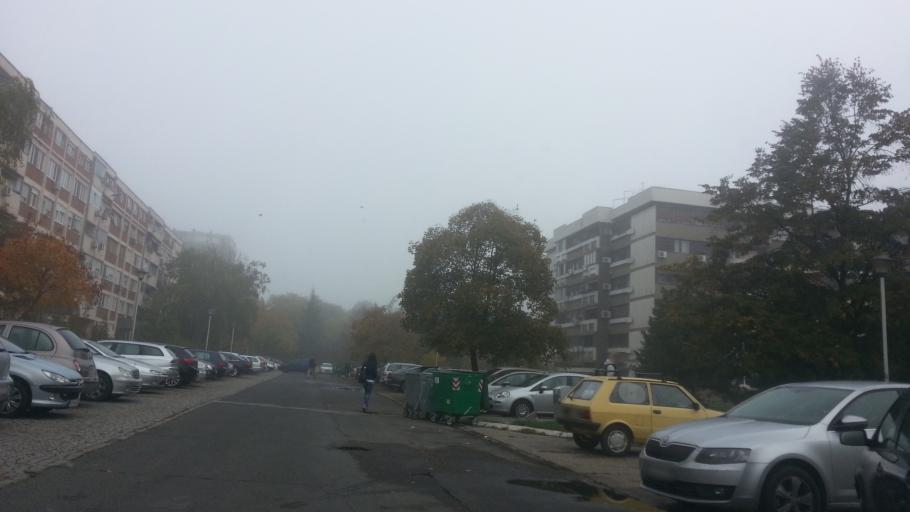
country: RS
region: Central Serbia
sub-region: Belgrade
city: Zemun
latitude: 44.8266
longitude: 20.4162
